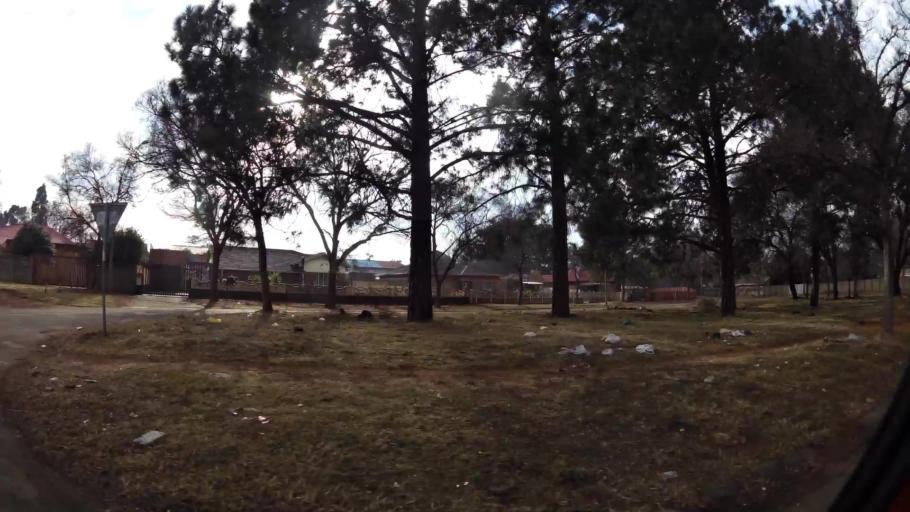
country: ZA
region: Gauteng
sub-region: Sedibeng District Municipality
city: Vanderbijlpark
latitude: -26.6985
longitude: 27.8130
